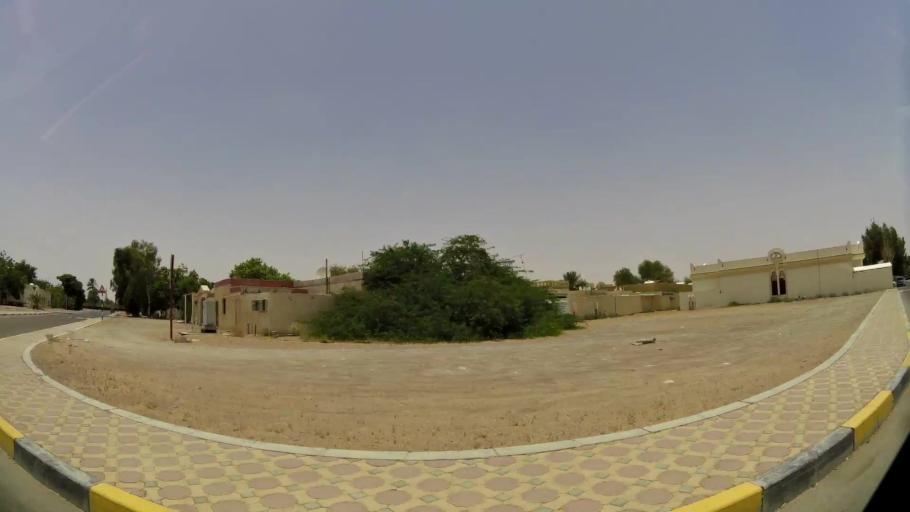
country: AE
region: Abu Dhabi
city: Al Ain
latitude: 24.2188
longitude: 55.7347
